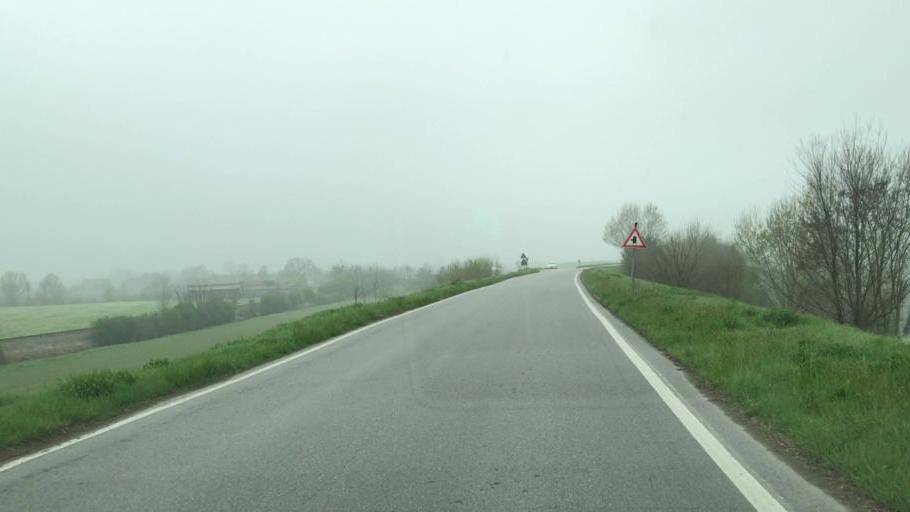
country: IT
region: Lombardy
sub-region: Provincia di Mantova
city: San Benedetto Po
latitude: 45.0369
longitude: 10.9229
